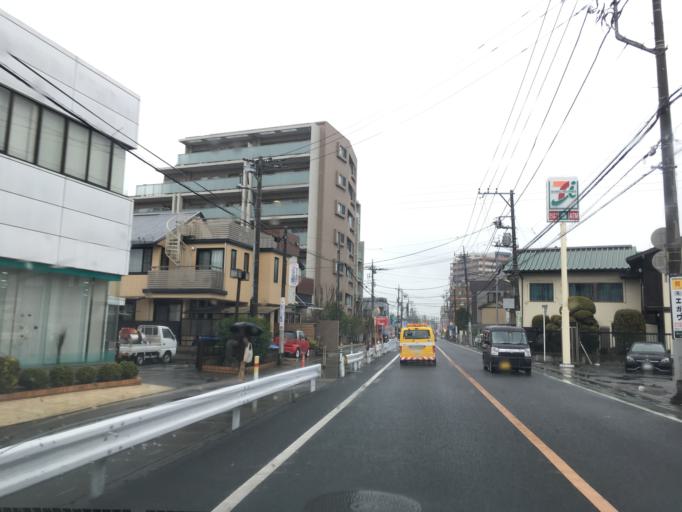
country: JP
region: Saitama
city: Koshigaya
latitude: 35.8852
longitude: 139.7837
